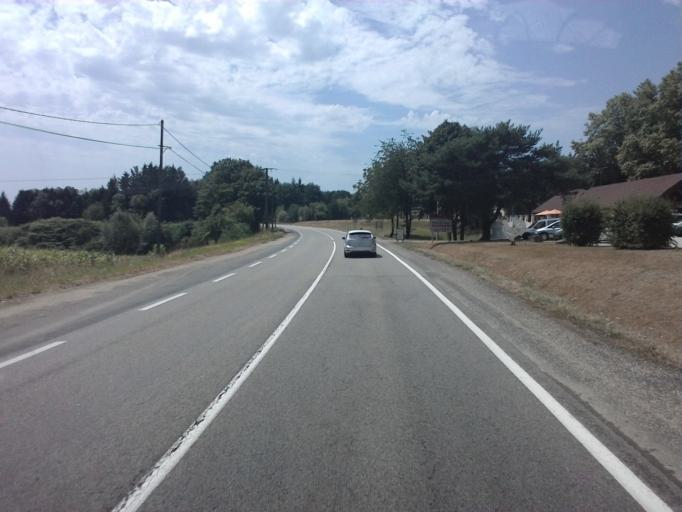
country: FR
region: Rhone-Alpes
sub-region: Departement de l'Ain
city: Coligny
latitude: 46.3619
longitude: 5.3300
